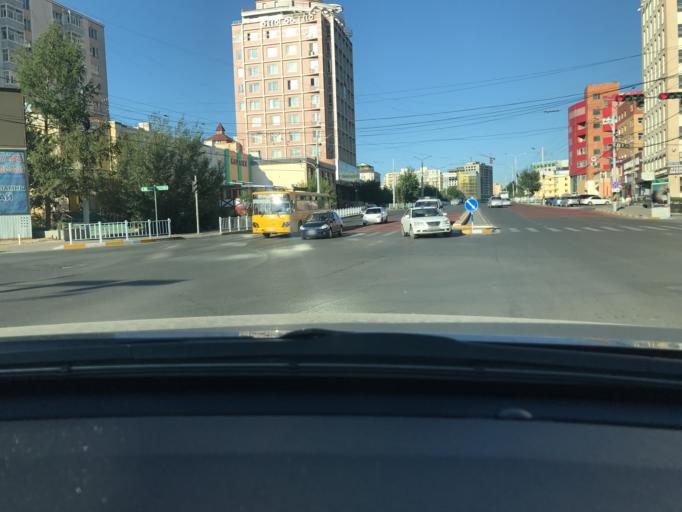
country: MN
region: Ulaanbaatar
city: Ulaanbaatar
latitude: 47.9185
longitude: 106.9352
